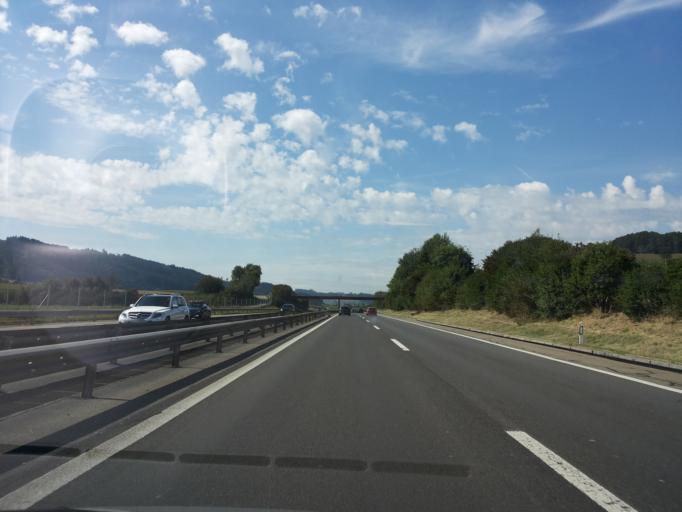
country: CH
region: Lucerne
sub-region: Willisau District
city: Wauwil
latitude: 47.2083
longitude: 8.0193
